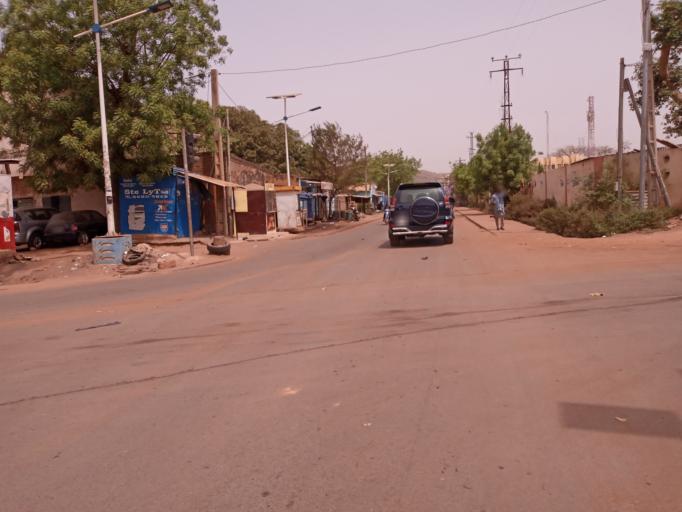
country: ML
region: Bamako
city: Bamako
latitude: 12.6466
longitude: -7.9802
